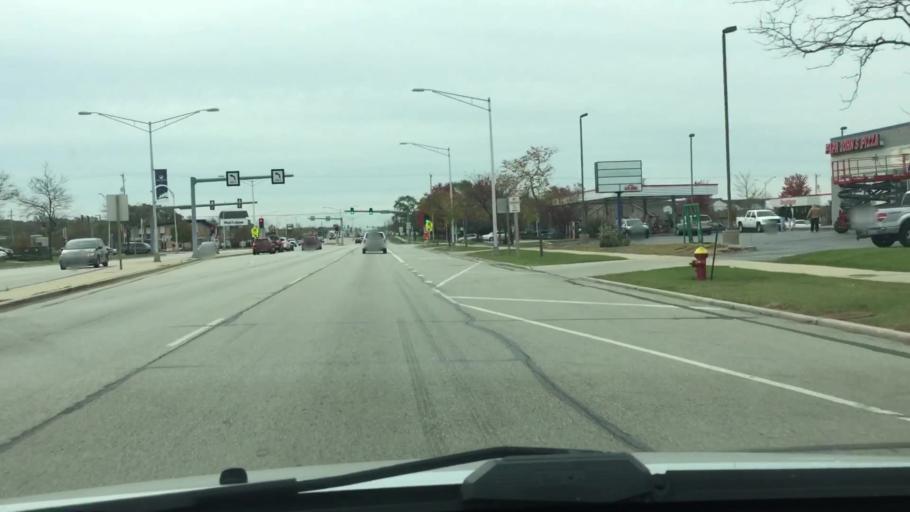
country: US
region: Wisconsin
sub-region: Milwaukee County
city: Oak Creek
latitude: 42.8880
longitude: -87.9123
